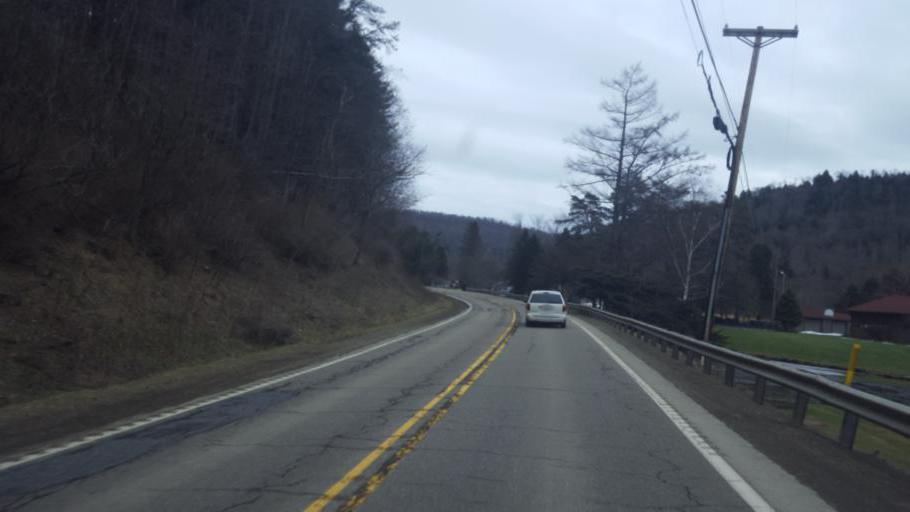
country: US
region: Pennsylvania
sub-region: Potter County
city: Coudersport
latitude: 41.8124
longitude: -77.9952
